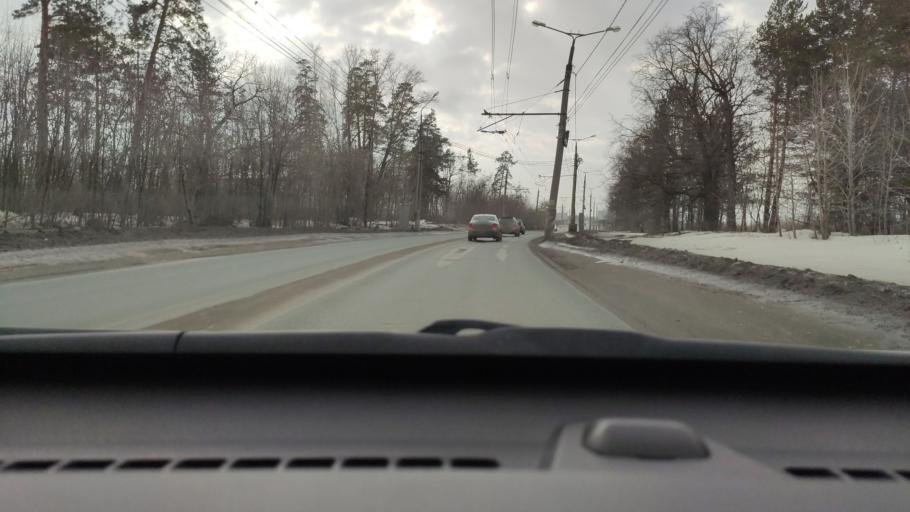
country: RU
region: Samara
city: Tol'yatti
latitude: 53.4894
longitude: 49.3818
